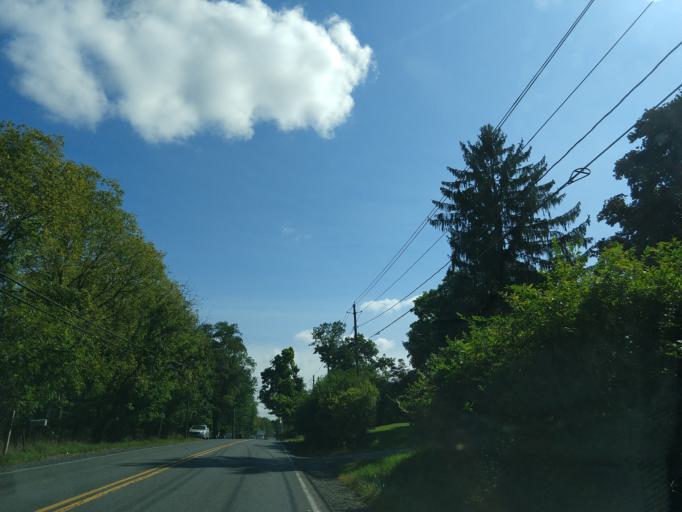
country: US
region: New York
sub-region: Tompkins County
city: South Hill
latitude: 42.4283
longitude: -76.4904
